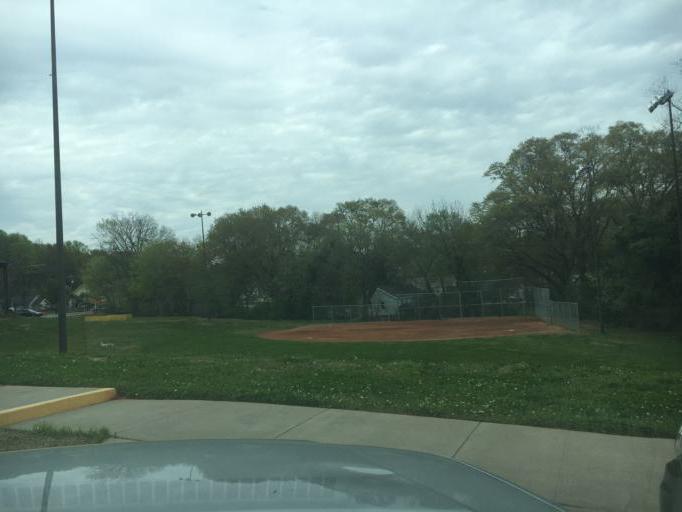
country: US
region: South Carolina
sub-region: Greenville County
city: Greenville
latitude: 34.8622
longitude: -82.3810
